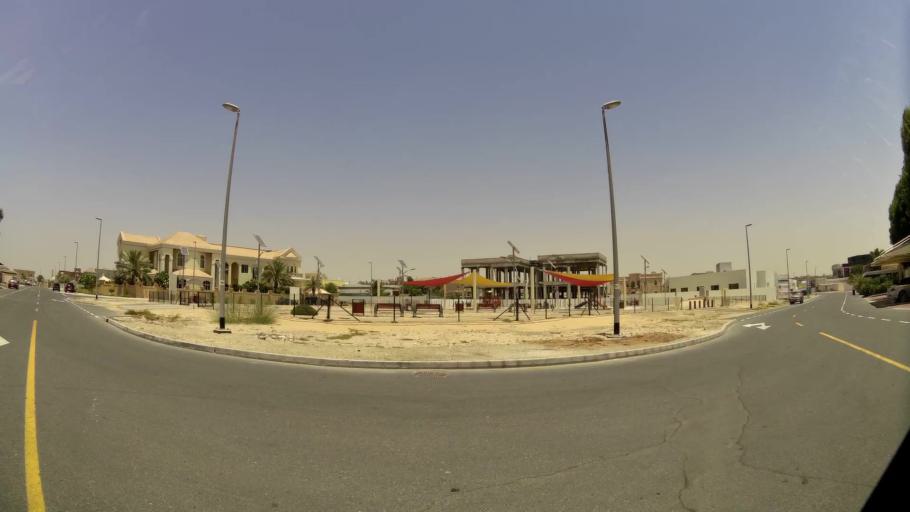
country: AE
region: Dubai
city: Dubai
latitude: 25.0916
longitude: 55.1905
